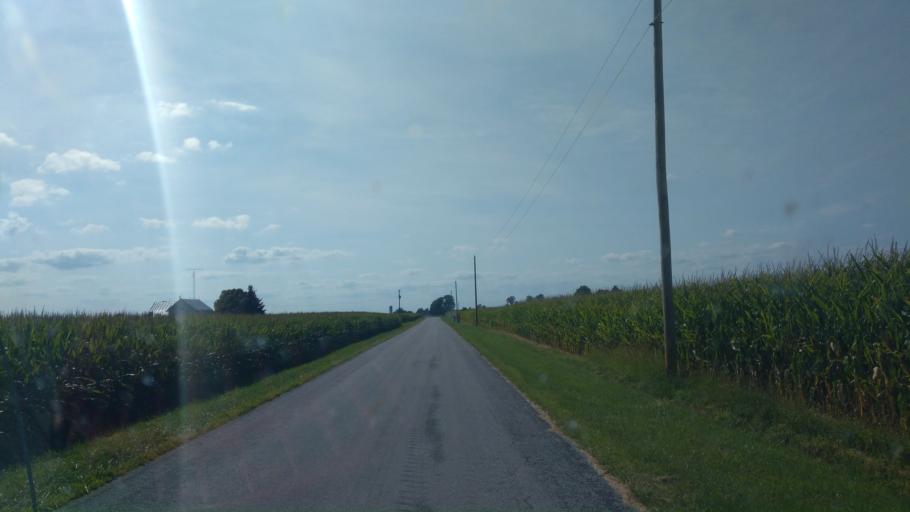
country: US
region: Ohio
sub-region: Hardin County
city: Forest
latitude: 40.6876
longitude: -83.4454
